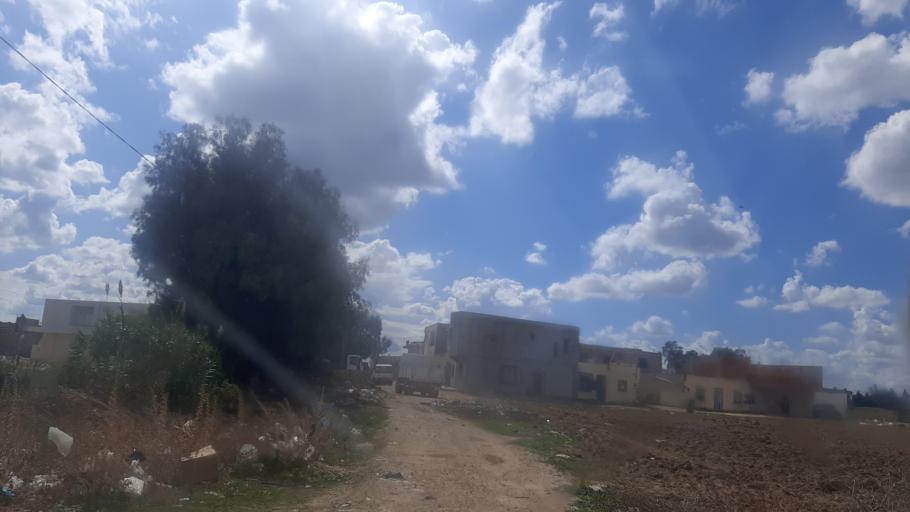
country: TN
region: Nabul
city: Korba
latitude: 36.5920
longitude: 10.8567
